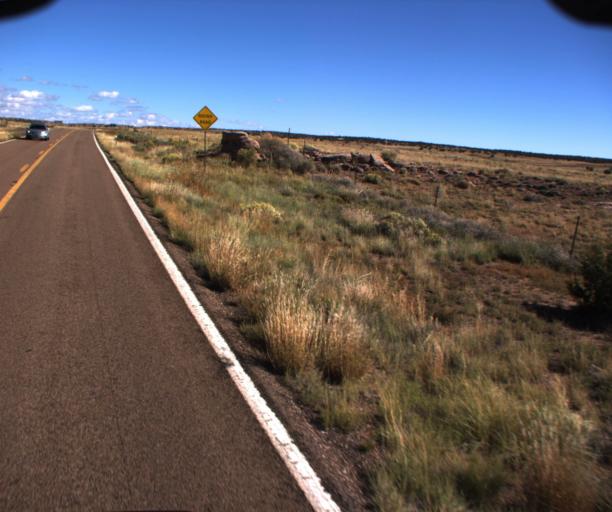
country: US
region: Arizona
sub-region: Apache County
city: Saint Johns
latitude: 34.6368
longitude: -109.3089
